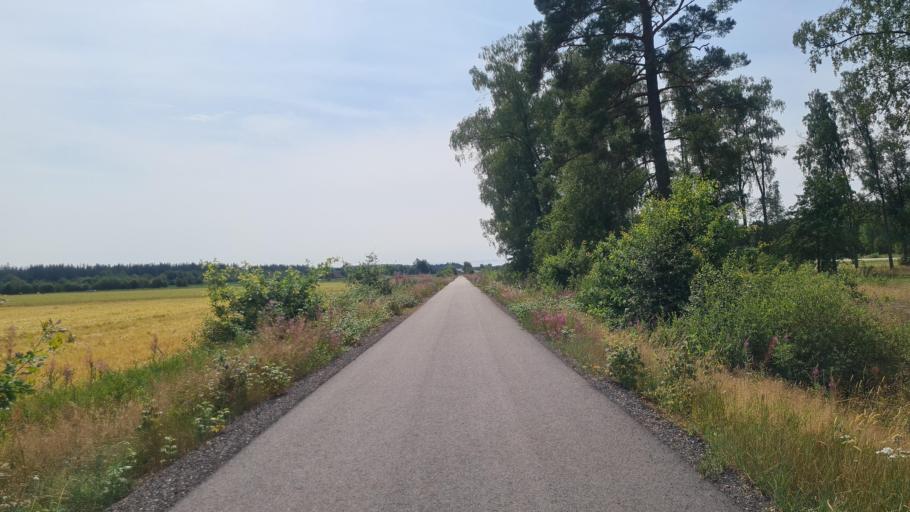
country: SE
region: Kronoberg
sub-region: Ljungby Kommun
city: Lagan
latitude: 56.8814
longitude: 13.9841
